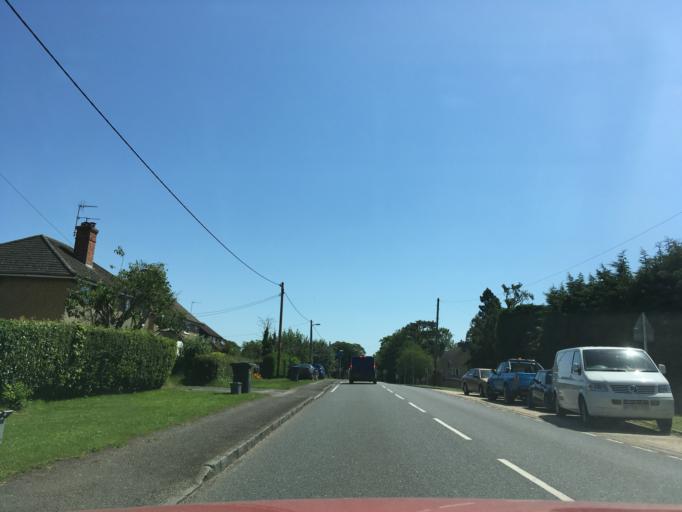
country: GB
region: England
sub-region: Northamptonshire
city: Brackley
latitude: 51.9974
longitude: -1.2009
